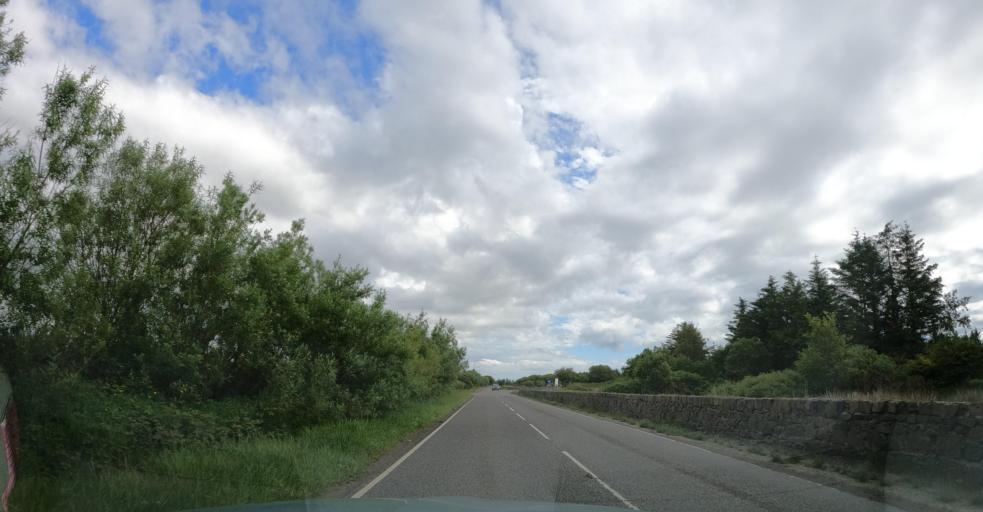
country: GB
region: Scotland
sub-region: Eilean Siar
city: Isle of Lewis
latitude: 58.2122
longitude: -6.4166
